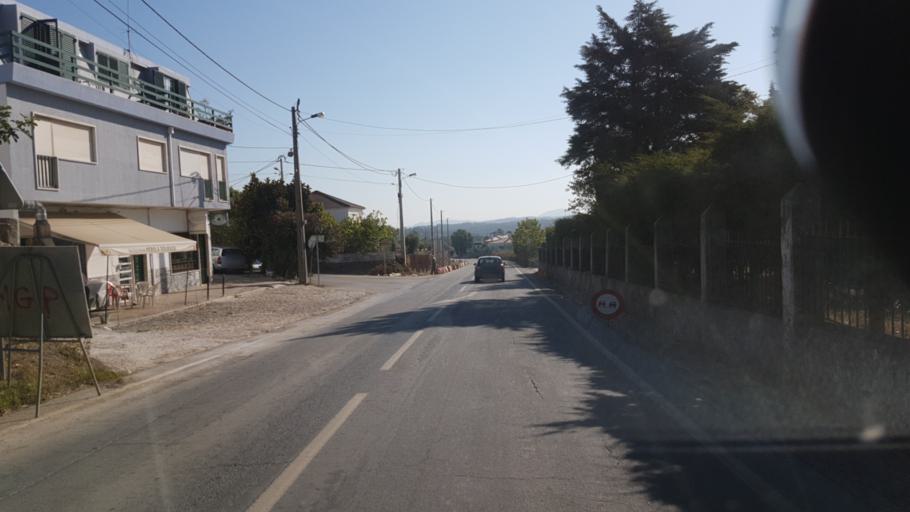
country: PT
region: Setubal
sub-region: Sesimbra
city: Sesimbra
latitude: 38.4665
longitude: -9.0954
